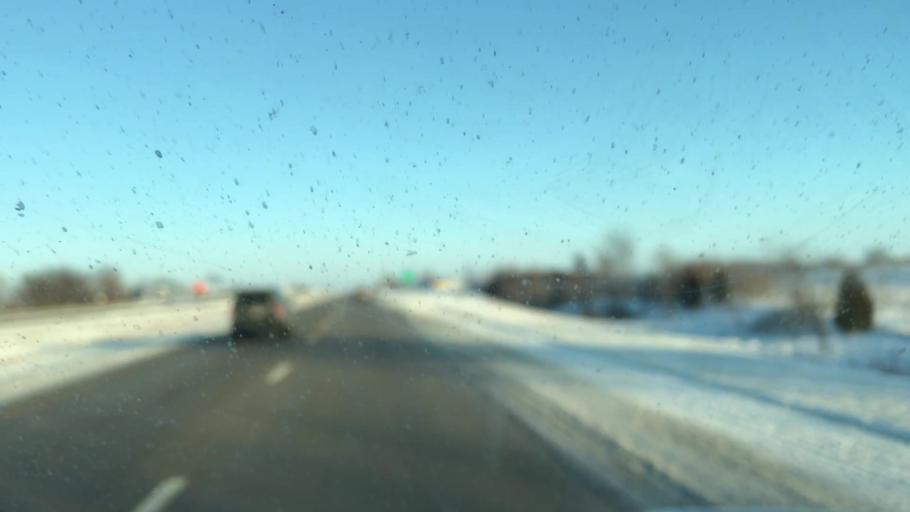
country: US
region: Missouri
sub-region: Andrew County
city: Country Club Village
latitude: 39.7476
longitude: -94.6986
